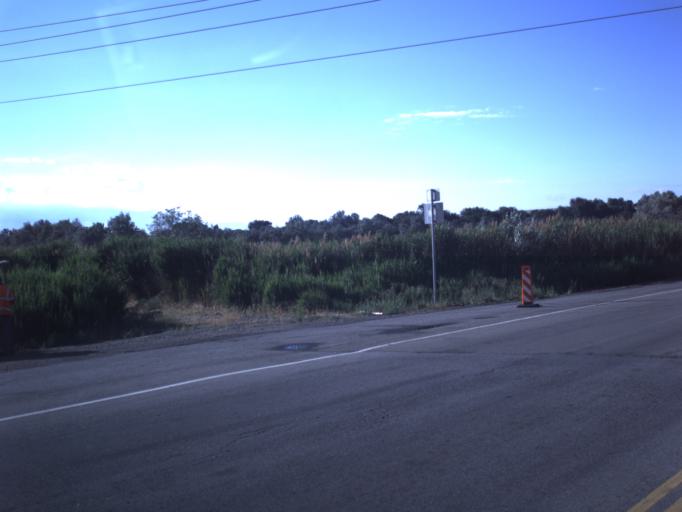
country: US
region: Utah
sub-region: Salt Lake County
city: Magna
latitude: 40.7164
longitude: -112.0918
